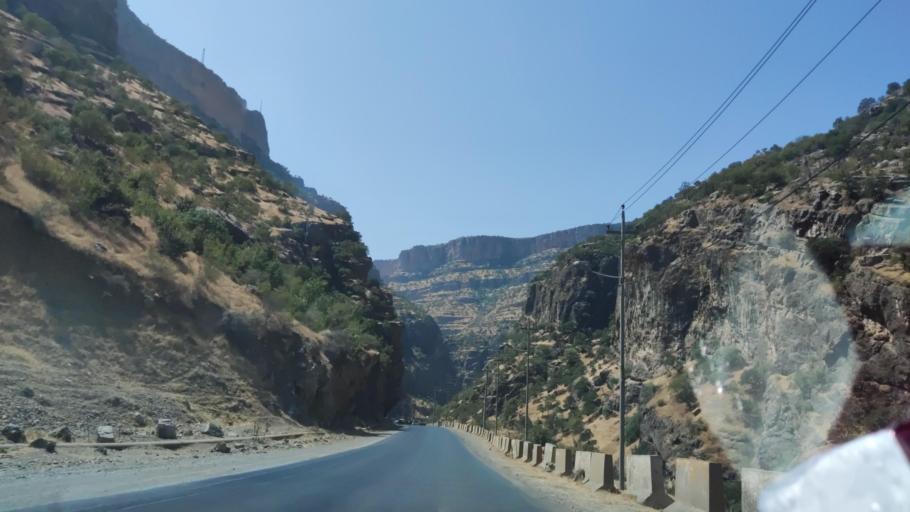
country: IQ
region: Arbil
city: Ruwandiz
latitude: 36.6404
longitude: 44.4922
